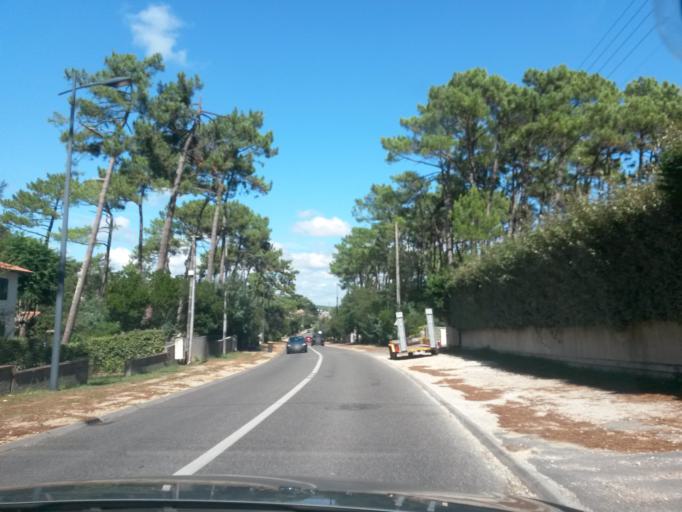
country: FR
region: Aquitaine
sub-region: Departement de la Gironde
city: Arcachon
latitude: 44.6952
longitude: -1.2337
